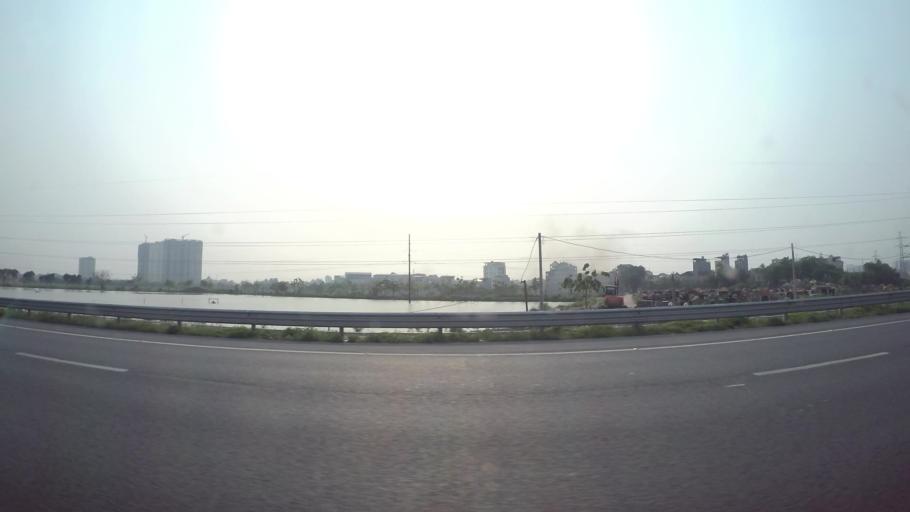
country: VN
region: Ha Noi
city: Van Dien
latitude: 20.9381
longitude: 105.8593
